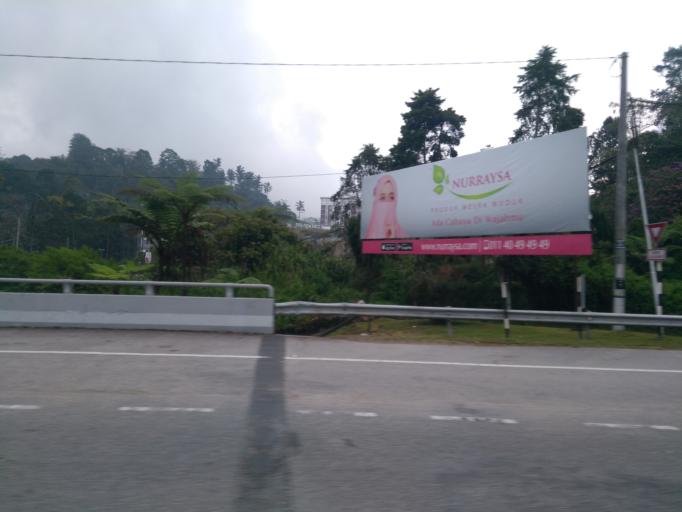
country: MY
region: Pahang
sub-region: Cameron Highlands
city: Tanah Rata
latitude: 4.4860
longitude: 101.3774
